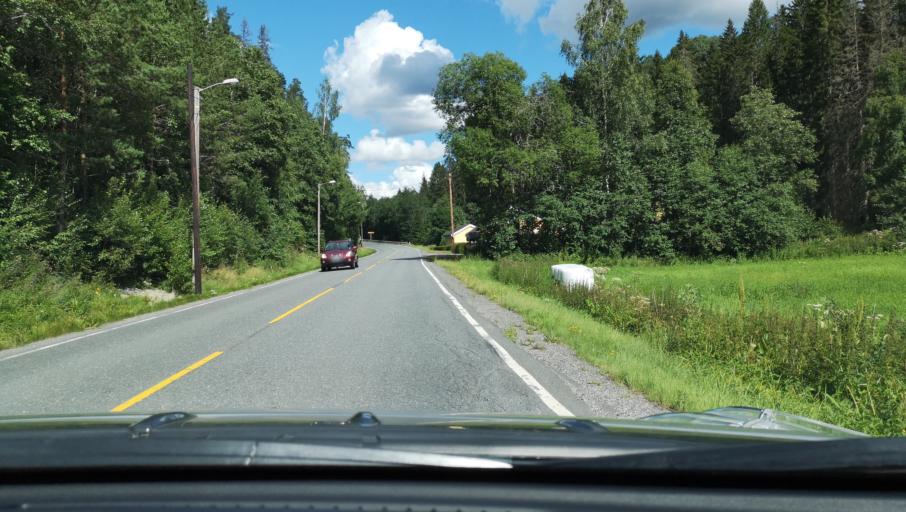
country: NO
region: Ostfold
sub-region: Hobol
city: Tomter
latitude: 59.6524
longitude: 10.9973
